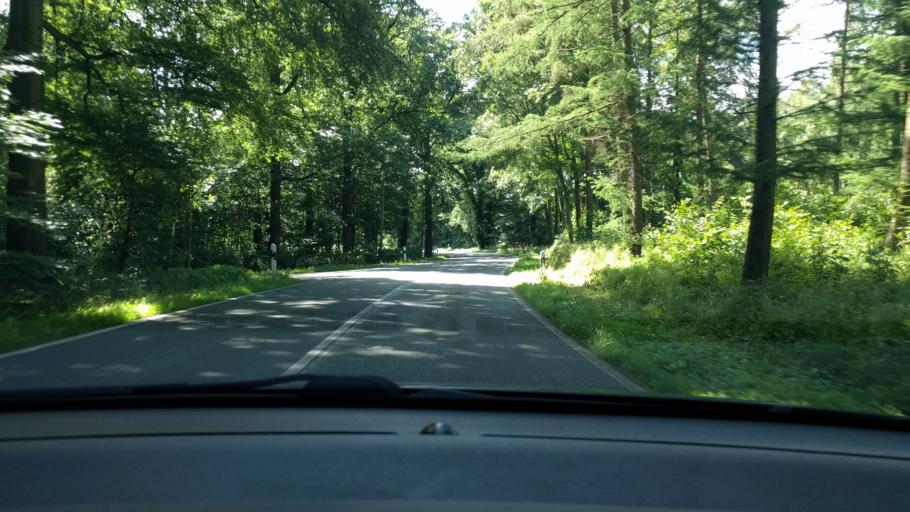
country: DE
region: North Rhine-Westphalia
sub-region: Regierungsbezirk Munster
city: Haltern
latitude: 51.7267
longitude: 7.2491
